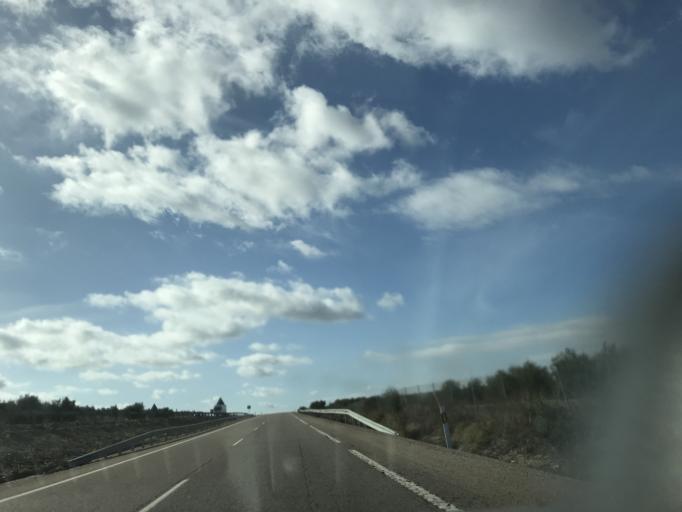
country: ES
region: Andalusia
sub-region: Provincia de Jaen
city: Lopera
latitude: 38.0059
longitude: -4.2313
